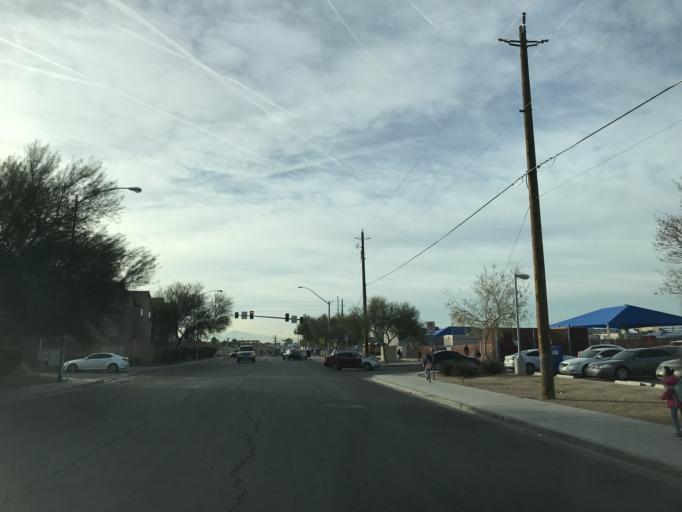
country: US
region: Nevada
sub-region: Clark County
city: Nellis Air Force Base
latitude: 36.2393
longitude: -115.0666
